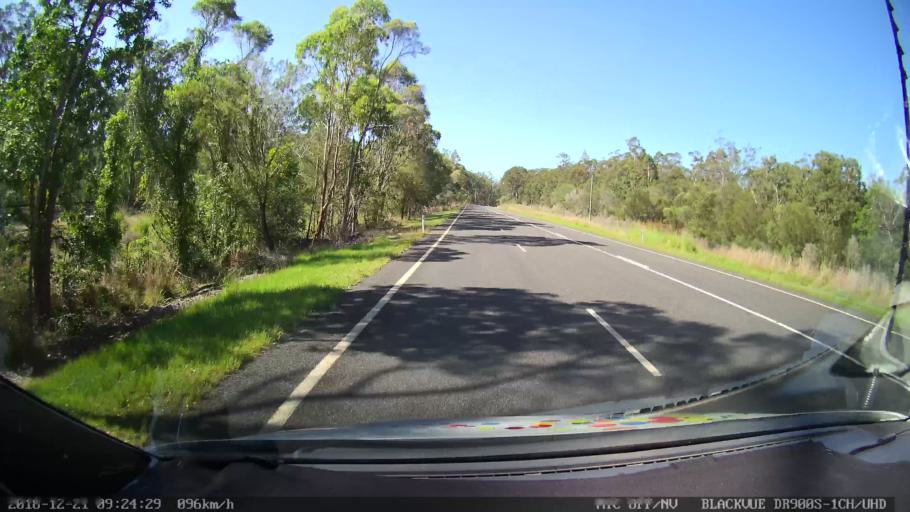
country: AU
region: New South Wales
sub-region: Clarence Valley
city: Maclean
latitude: -29.3681
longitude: 153.0160
